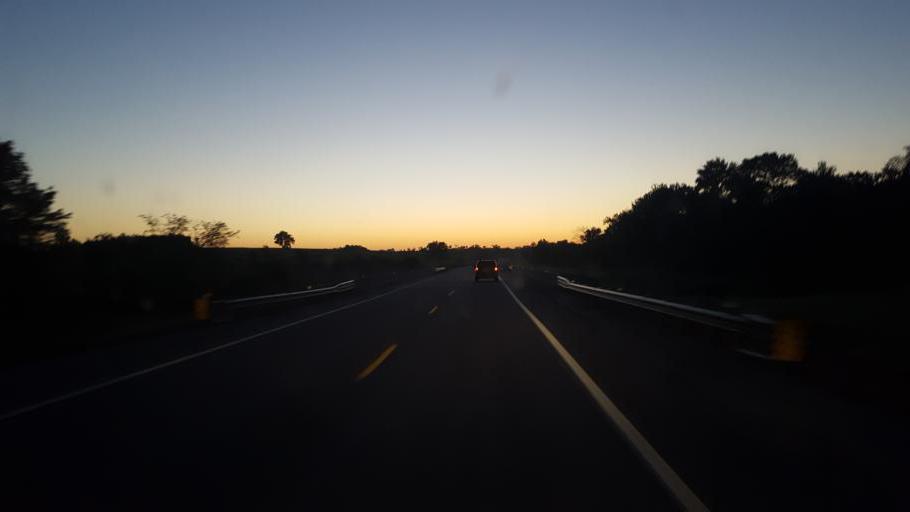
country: US
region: Missouri
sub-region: Putnam County
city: Terre Haute
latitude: 40.4587
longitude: -93.4044
